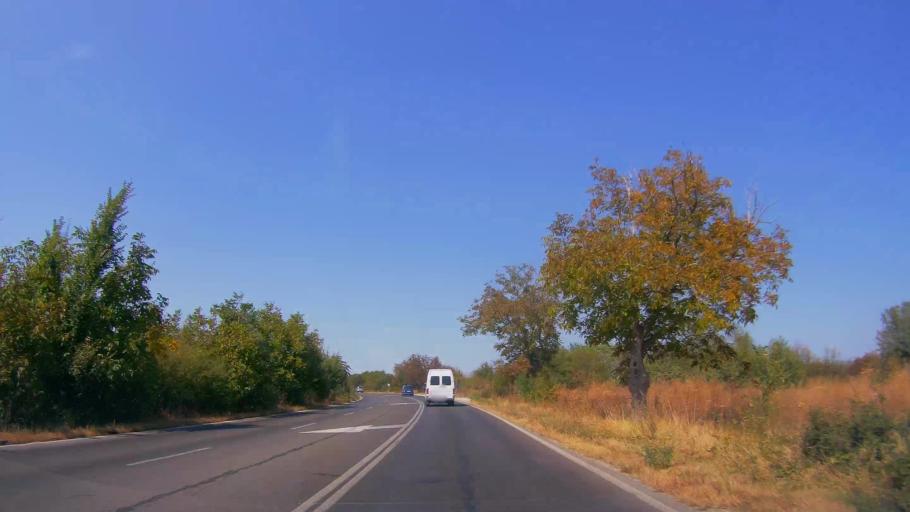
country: BG
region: Razgrad
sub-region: Obshtina Tsar Kaloyan
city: Tsar Kaloyan
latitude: 43.6337
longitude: 26.2007
